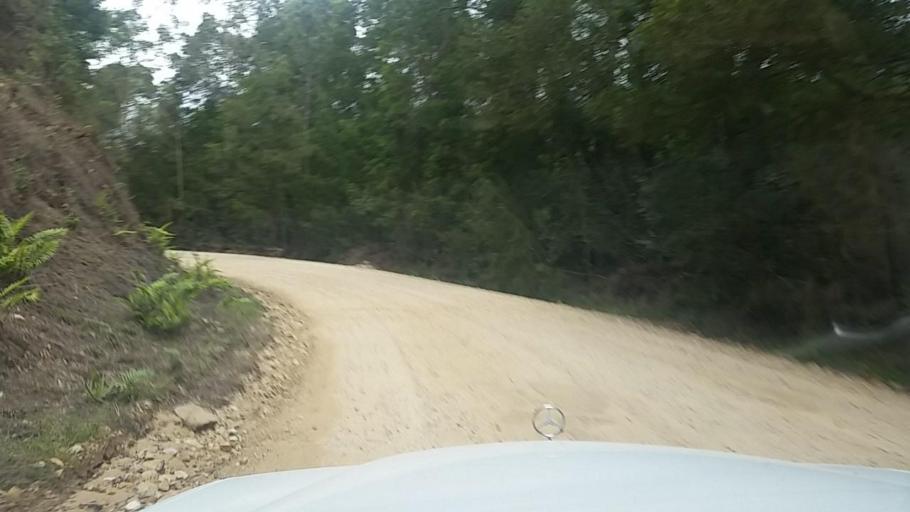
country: ZA
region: Western Cape
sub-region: Eden District Municipality
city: Knysna
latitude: -34.0022
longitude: 23.1167
